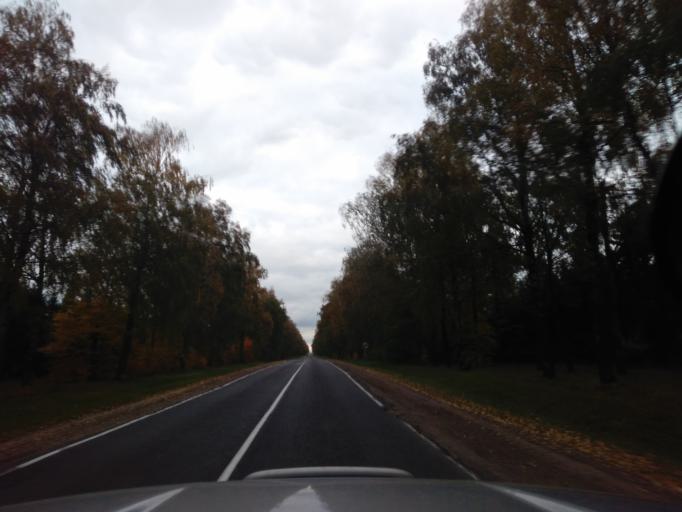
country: BY
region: Minsk
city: Slutsk
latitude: 53.2176
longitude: 27.4277
